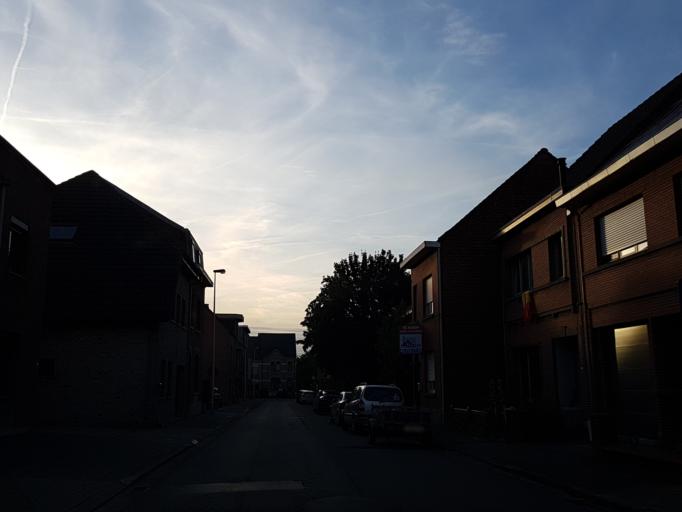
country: BE
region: Flanders
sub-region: Provincie Vlaams-Brabant
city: Londerzeel
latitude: 51.0048
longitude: 4.3058
